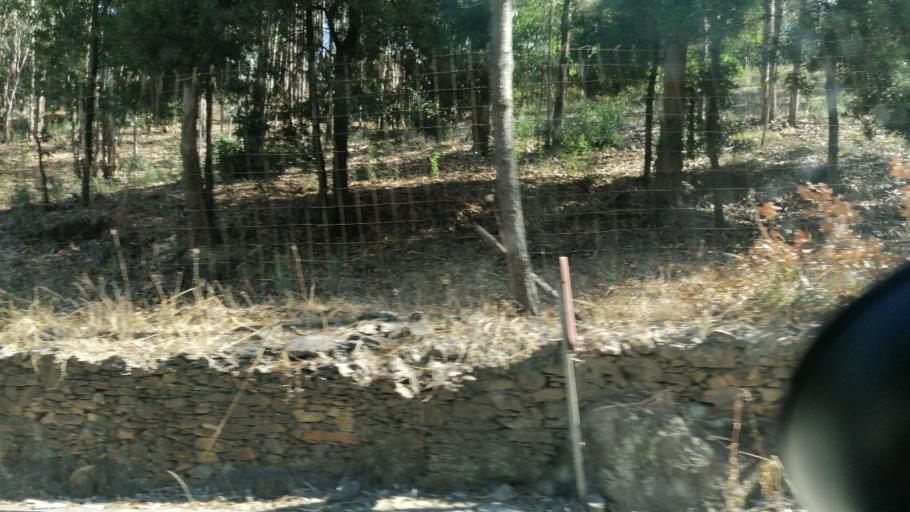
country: PT
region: Porto
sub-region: Trofa
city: Bougado
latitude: 41.3393
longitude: -8.5225
